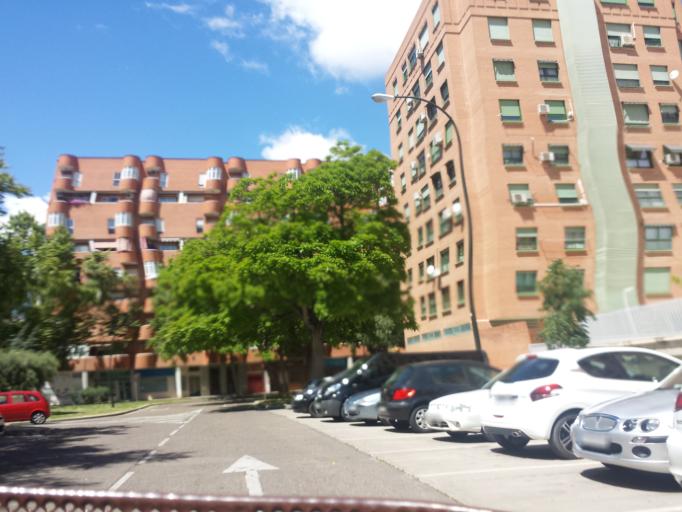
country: ES
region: Aragon
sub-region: Provincia de Zaragoza
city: Zaragoza
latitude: 41.6691
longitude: -0.8857
